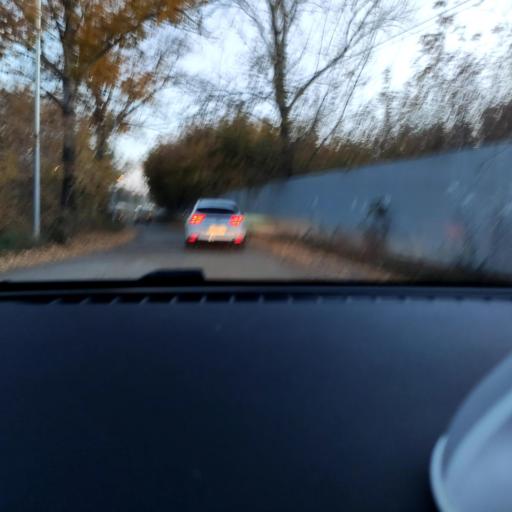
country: RU
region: Samara
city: Petra-Dubrava
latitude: 53.3157
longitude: 50.2927
